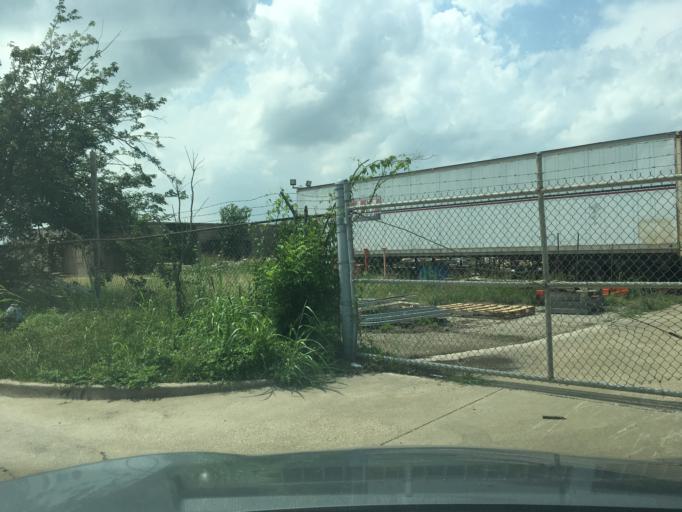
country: US
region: Texas
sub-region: Dallas County
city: Garland
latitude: 32.9112
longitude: -96.6740
